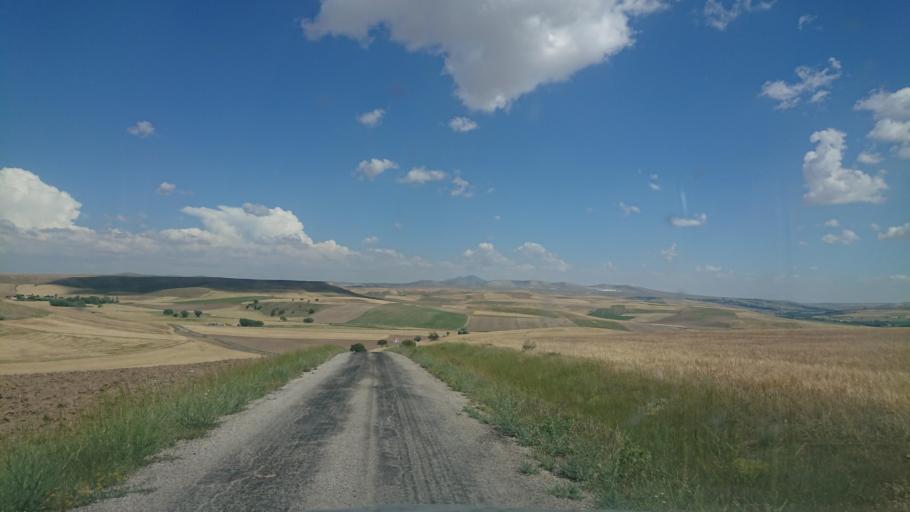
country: TR
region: Aksaray
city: Agacoren
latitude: 38.8018
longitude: 33.8141
